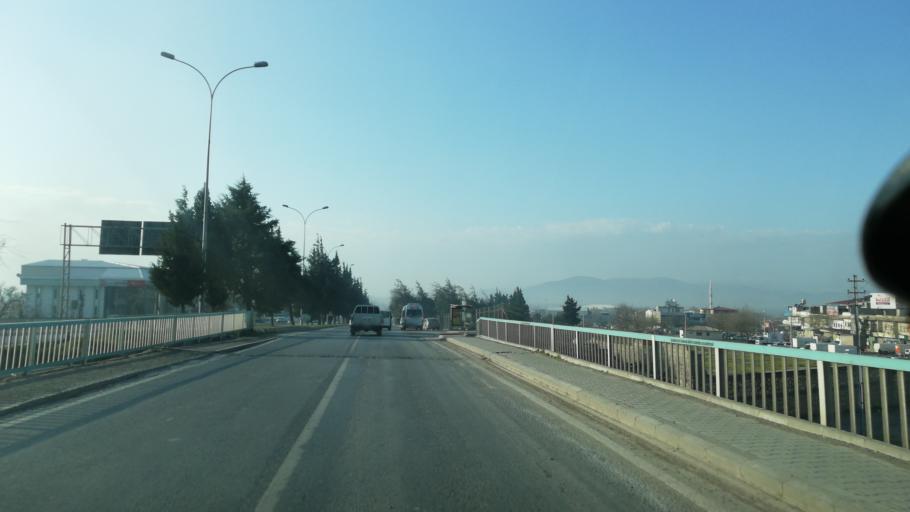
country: TR
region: Kahramanmaras
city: Kahramanmaras
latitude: 37.5661
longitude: 36.9243
